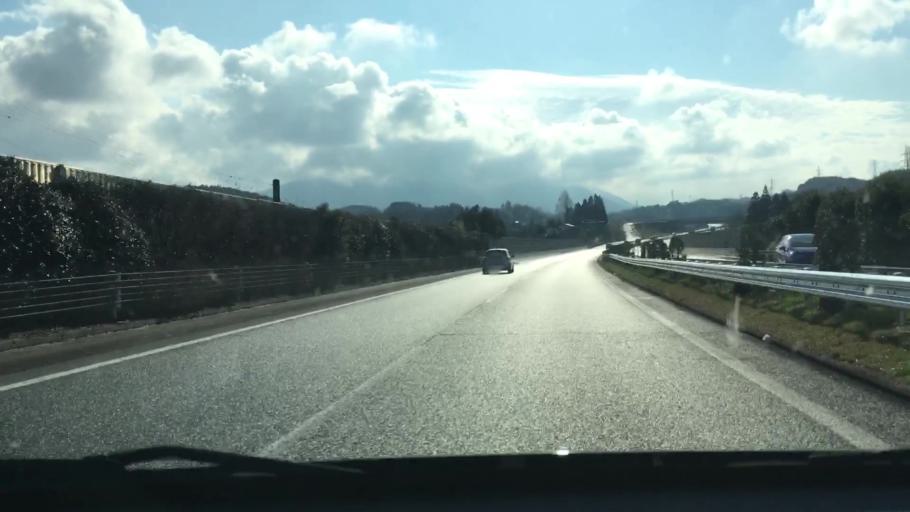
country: JP
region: Kumamoto
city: Matsubase
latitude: 32.5817
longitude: 130.7149
